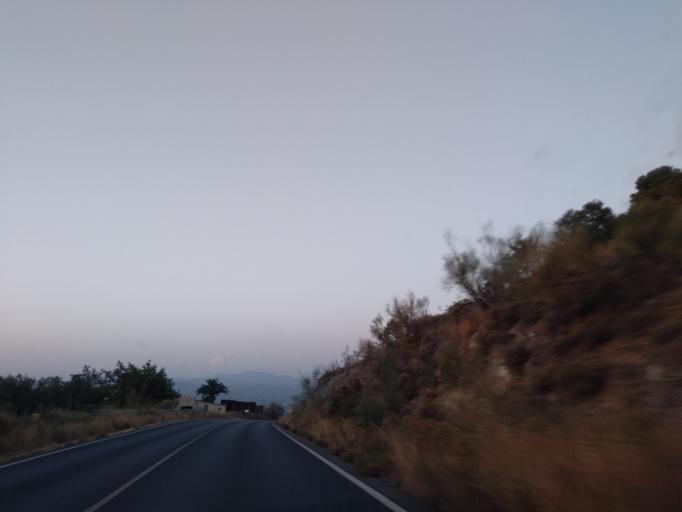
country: ES
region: Andalusia
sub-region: Provincia de Malaga
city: Cartama
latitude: 36.6972
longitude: -4.6505
